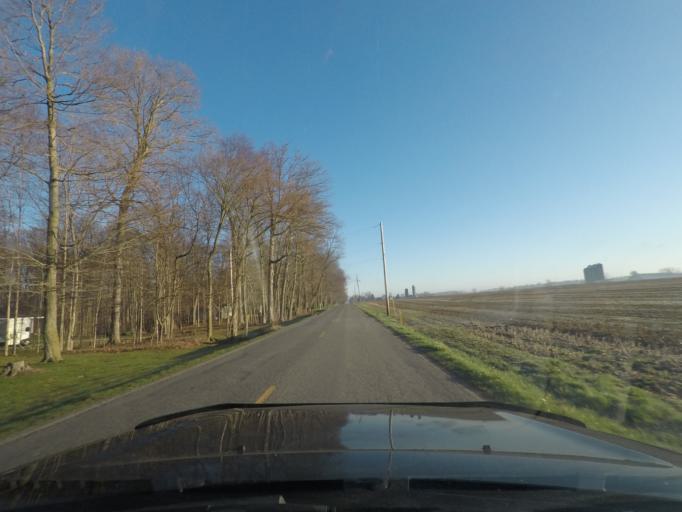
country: US
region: Indiana
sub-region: Elkhart County
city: Dunlap
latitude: 41.5735
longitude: -85.9251
